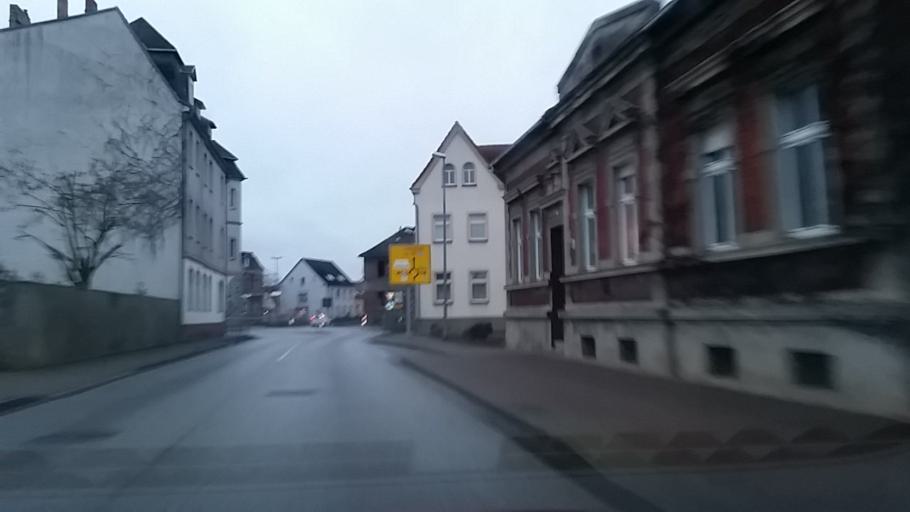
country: DE
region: Brandenburg
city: Perleberg
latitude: 53.0821
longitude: 11.8609
